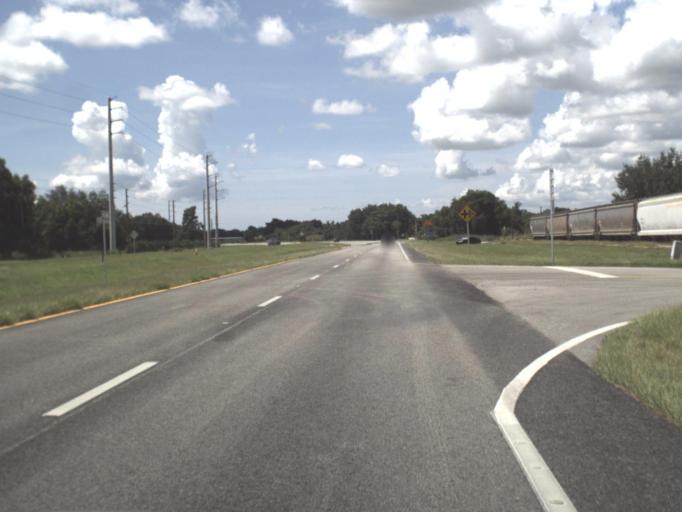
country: US
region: Florida
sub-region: DeSoto County
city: Nocatee
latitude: 27.0871
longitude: -81.9527
